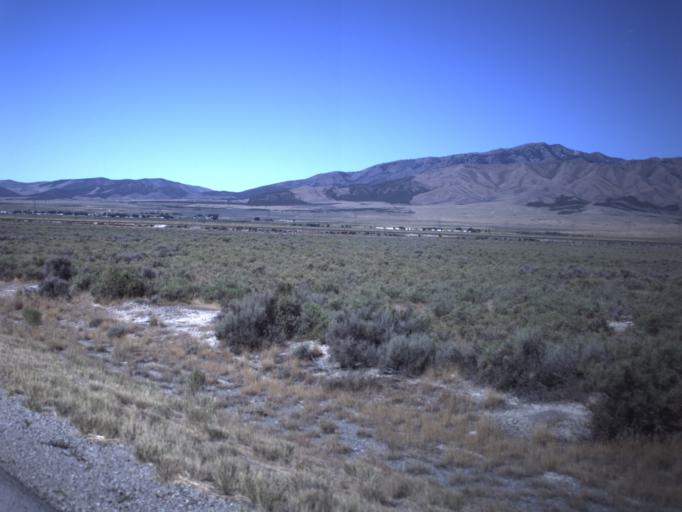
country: US
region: Utah
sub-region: Tooele County
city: Tooele
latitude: 40.3729
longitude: -112.3982
